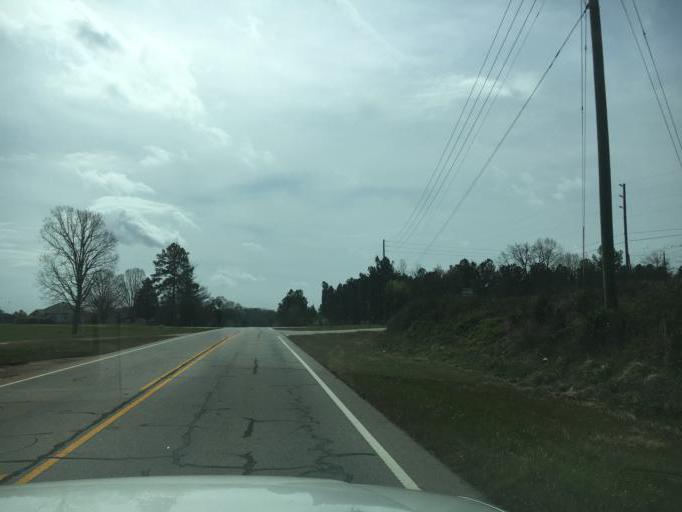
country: US
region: Georgia
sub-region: Franklin County
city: Gumlog
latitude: 34.4582
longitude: -83.0528
